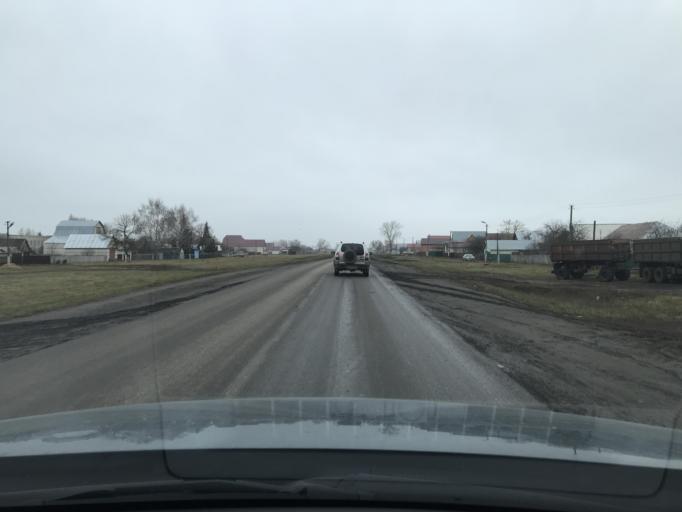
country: RU
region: Penza
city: Zemetchino
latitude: 53.5091
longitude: 42.6384
